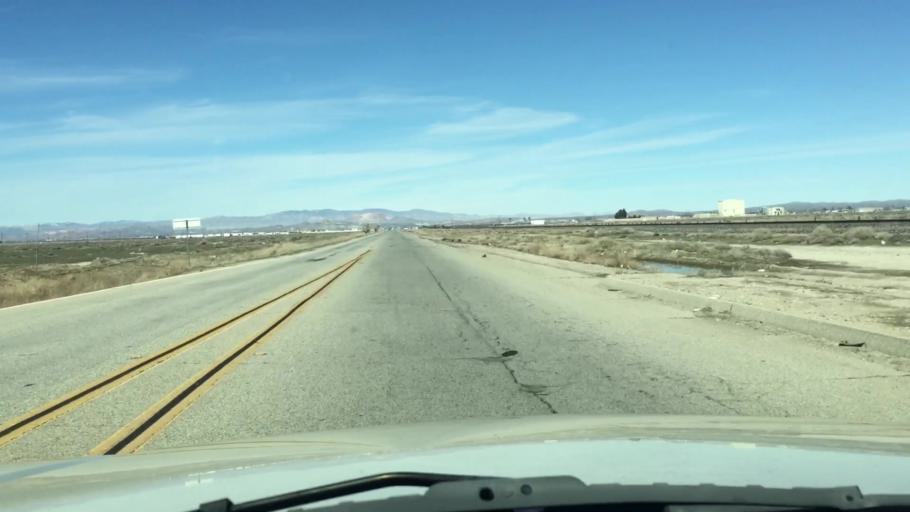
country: US
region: California
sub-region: Los Angeles County
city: Lancaster
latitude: 34.7241
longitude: -118.1407
